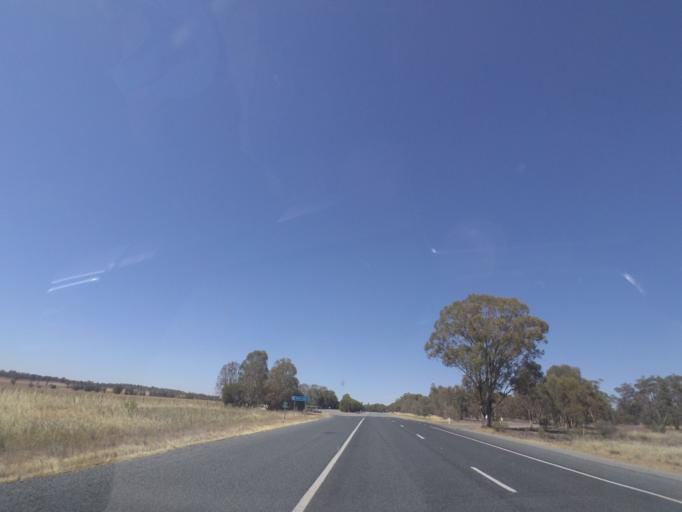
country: AU
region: New South Wales
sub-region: Narrandera
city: Narrandera
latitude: -34.4461
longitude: 146.8398
